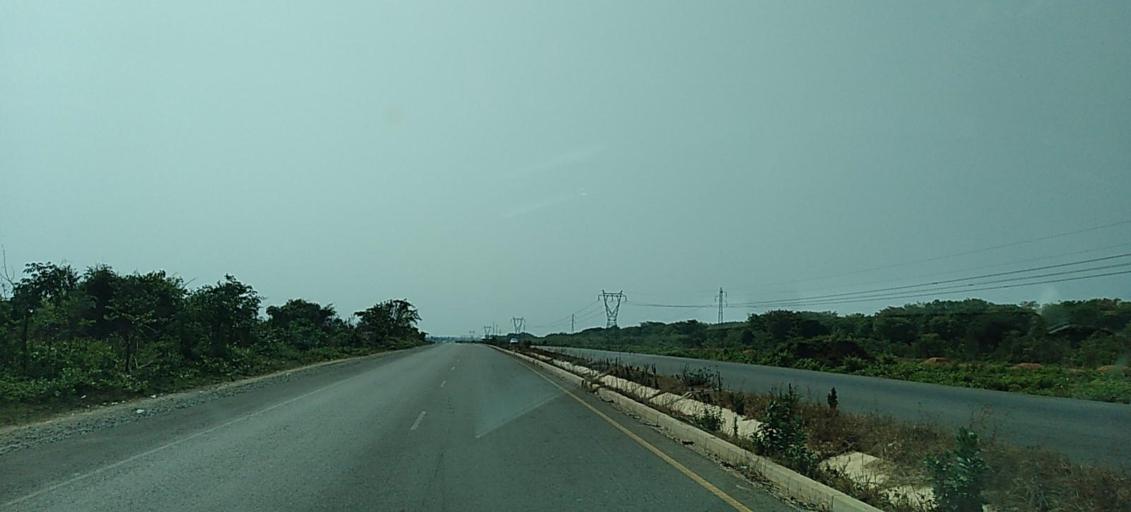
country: ZM
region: Copperbelt
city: Chingola
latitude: -12.5823
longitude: 27.9303
